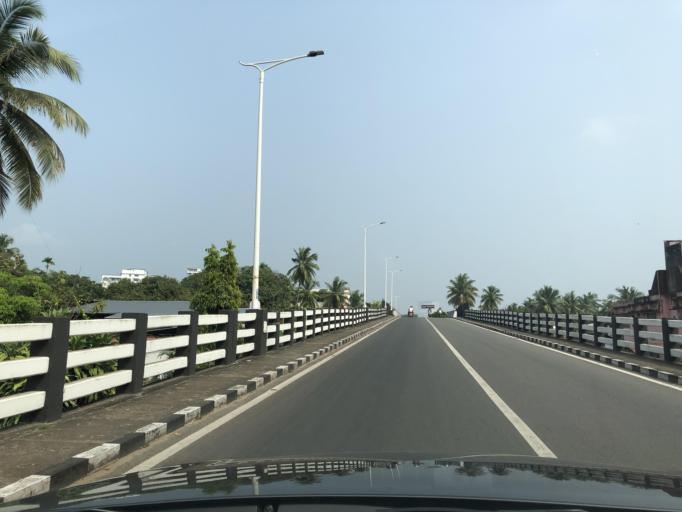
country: IN
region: Kerala
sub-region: Kozhikode
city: Kozhikode
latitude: 11.2639
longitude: 75.7735
